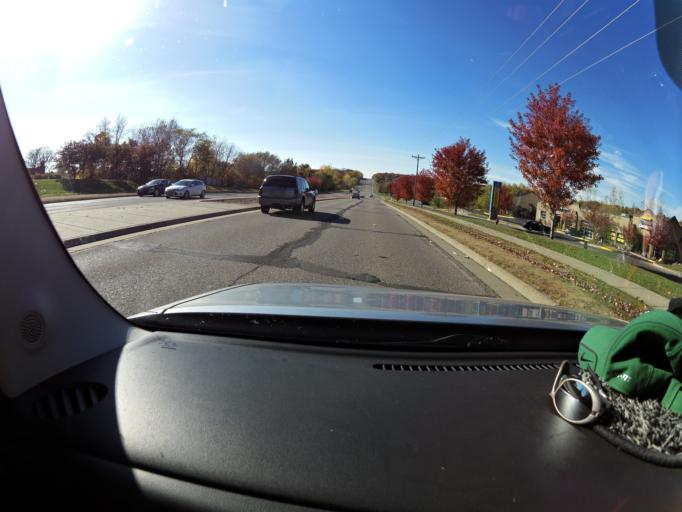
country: US
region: Minnesota
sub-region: Scott County
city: Prior Lake
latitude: 44.7464
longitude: -93.3864
